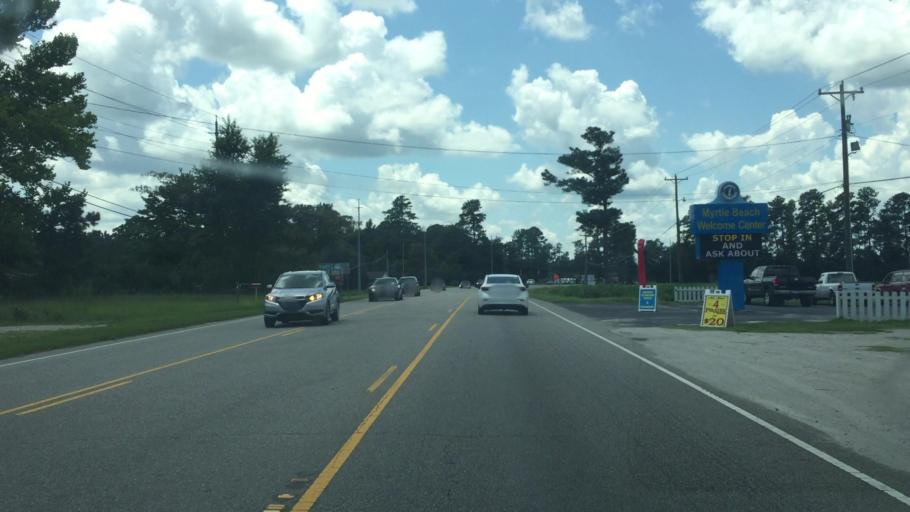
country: US
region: North Carolina
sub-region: Columbus County
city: Tabor City
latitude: 34.1603
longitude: -78.8479
